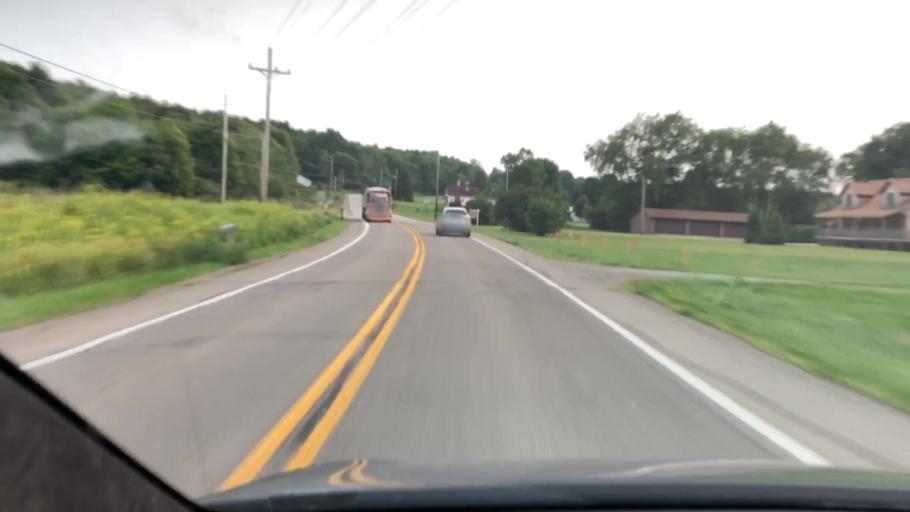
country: US
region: Pennsylvania
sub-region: Mercer County
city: Grove City
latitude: 41.1728
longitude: -79.9881
